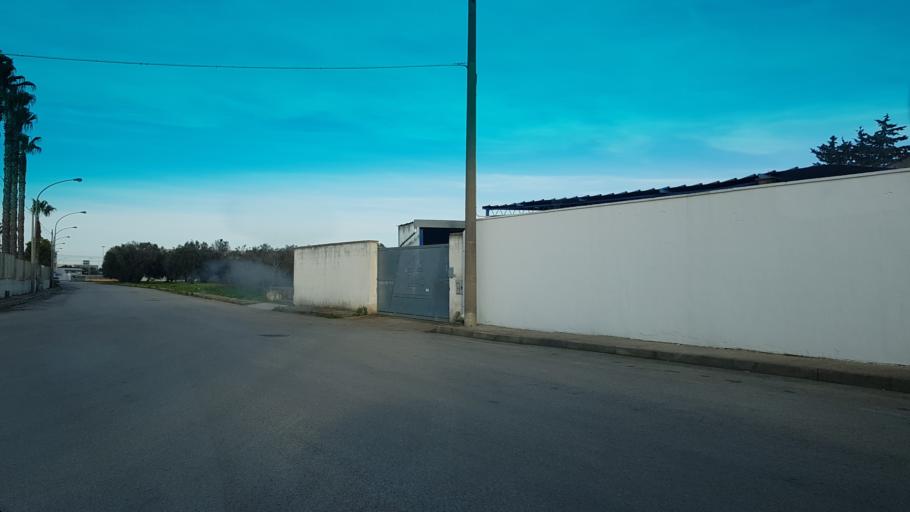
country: IT
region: Apulia
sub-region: Provincia di Brindisi
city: Mesagne
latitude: 40.5747
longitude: 17.8298
